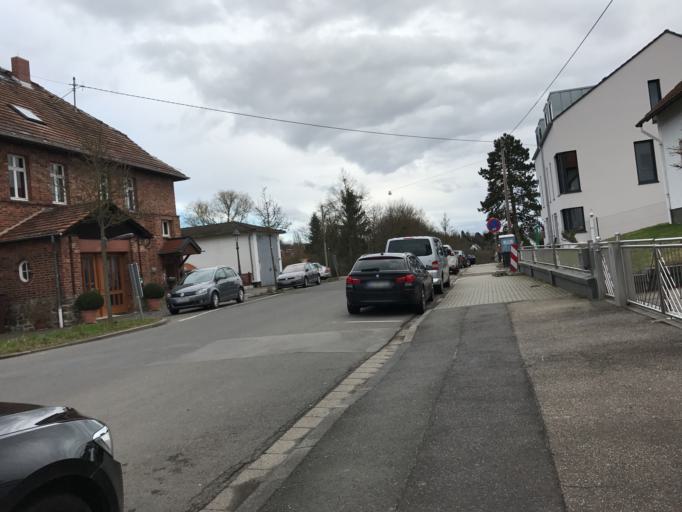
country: DE
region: Hesse
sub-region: Regierungsbezirk Darmstadt
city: Niedernhausen
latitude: 50.0825
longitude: 8.3251
